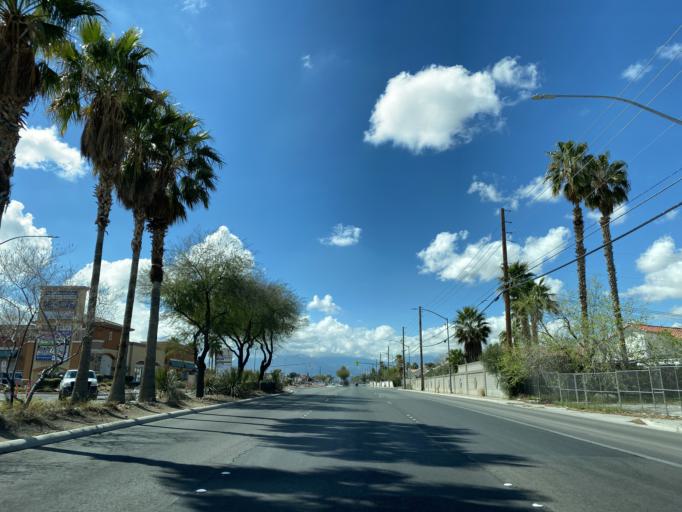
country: US
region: Nevada
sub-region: Clark County
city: North Las Vegas
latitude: 36.2395
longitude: -115.1829
